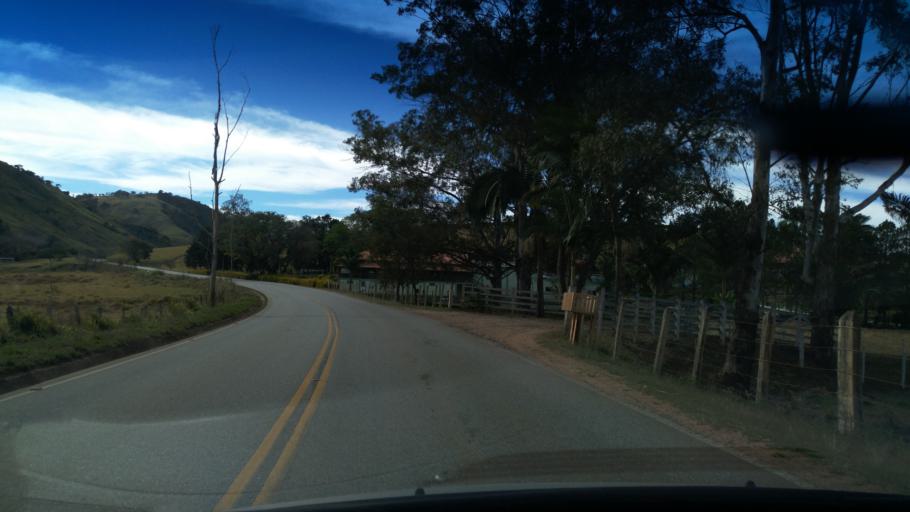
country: BR
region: Minas Gerais
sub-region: Andradas
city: Andradas
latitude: -22.0563
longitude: -46.4103
